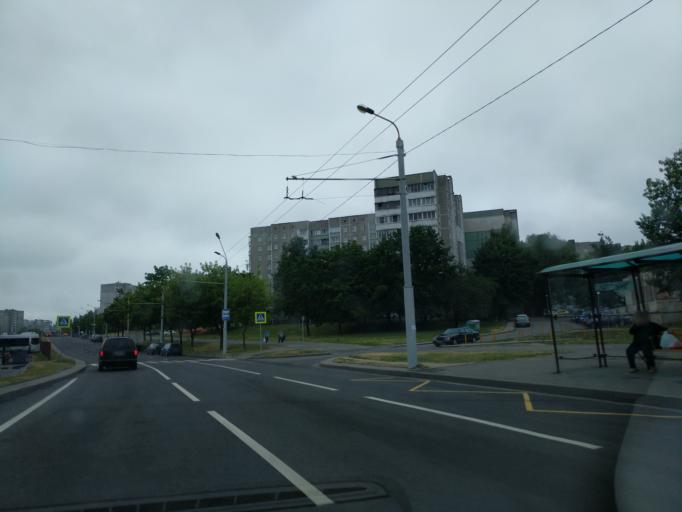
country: BY
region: Minsk
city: Novoye Medvezhino
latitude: 53.8625
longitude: 27.4659
